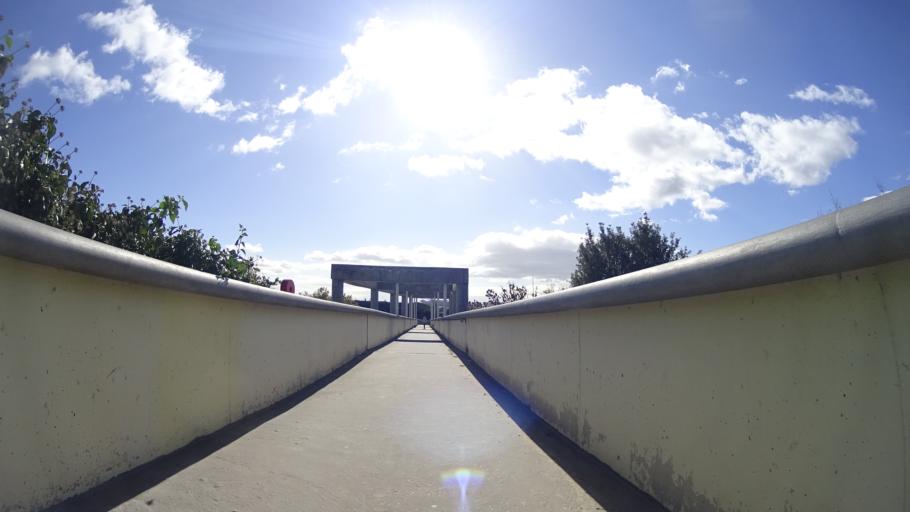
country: ES
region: Madrid
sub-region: Provincia de Madrid
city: San Blas
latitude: 40.4606
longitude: -3.6080
